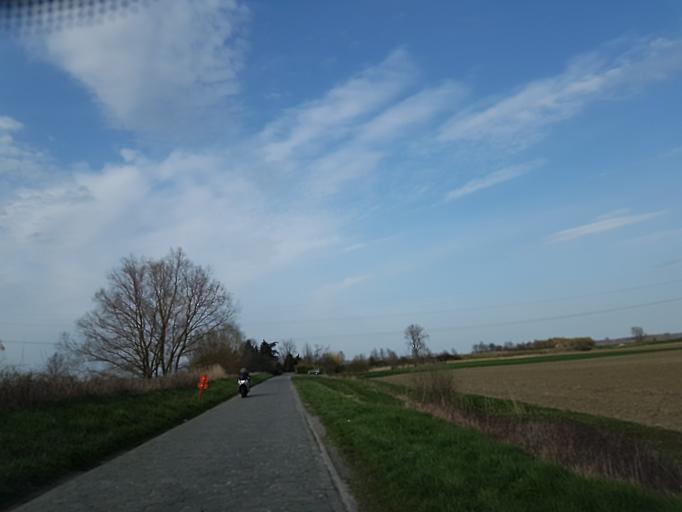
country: BE
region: Flanders
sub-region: Provincie Oost-Vlaanderen
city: Assenede
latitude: 51.2745
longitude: 3.7132
